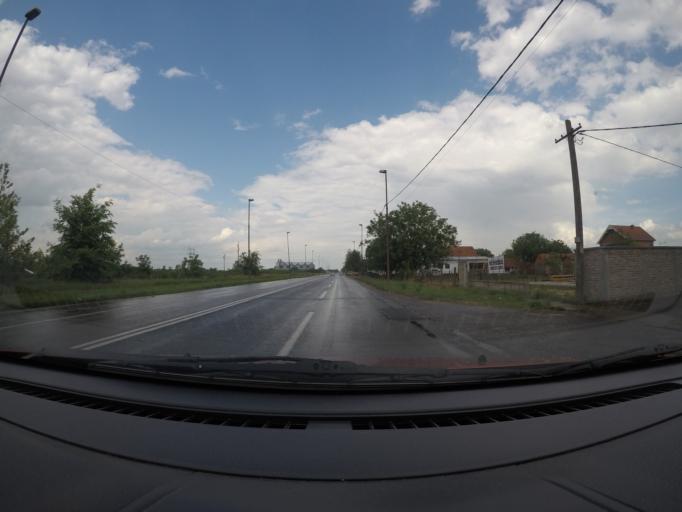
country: RS
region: Autonomna Pokrajina Vojvodina
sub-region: Srednjebanatski Okrug
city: Zrenjanin
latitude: 45.3898
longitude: 20.4263
